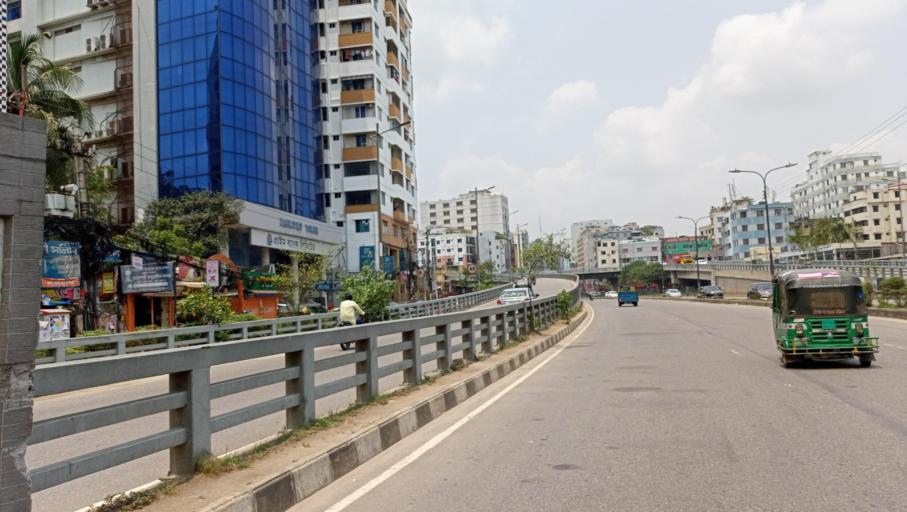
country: BD
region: Dhaka
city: Paltan
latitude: 23.7749
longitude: 90.4259
